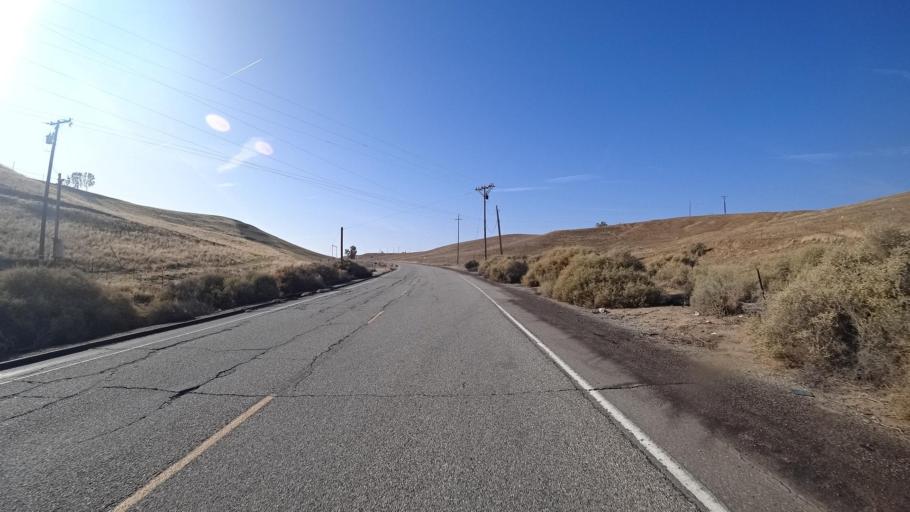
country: US
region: California
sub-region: Kern County
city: Oildale
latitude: 35.4997
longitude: -118.9940
